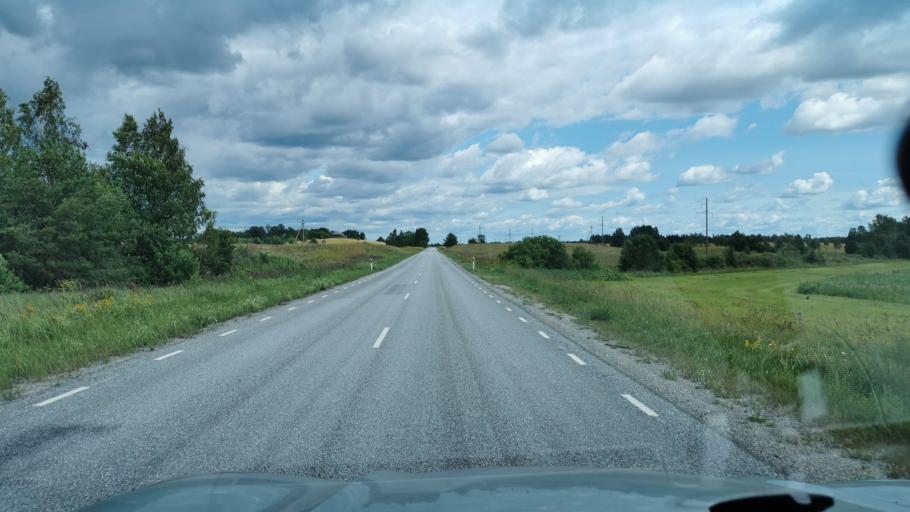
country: EE
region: Harju
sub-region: Kuusalu vald
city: Kuusalu
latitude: 59.2132
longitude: 25.6009
